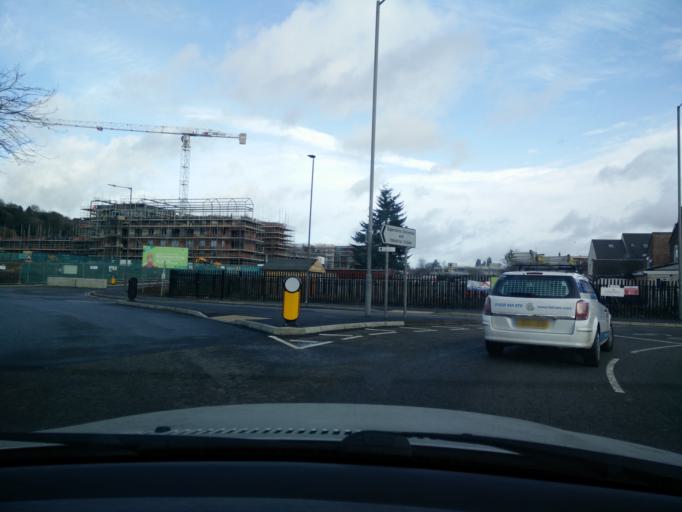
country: GB
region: England
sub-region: Buckinghamshire
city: High Wycombe
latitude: 51.6349
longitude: -0.7523
